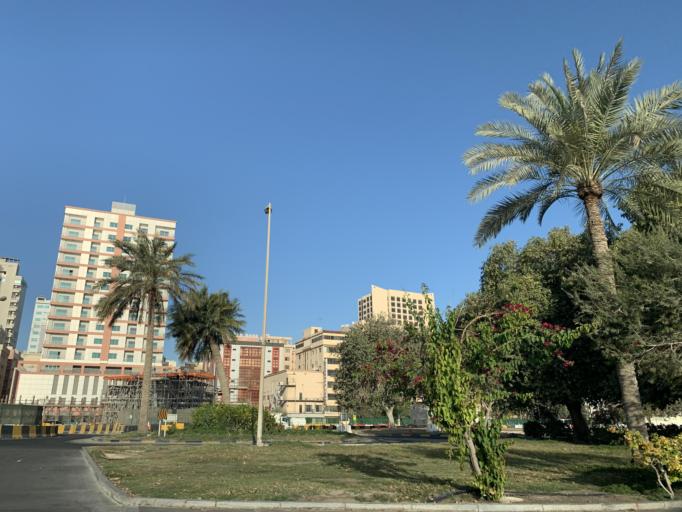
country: BH
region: Manama
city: Manama
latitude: 26.2334
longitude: 50.5995
